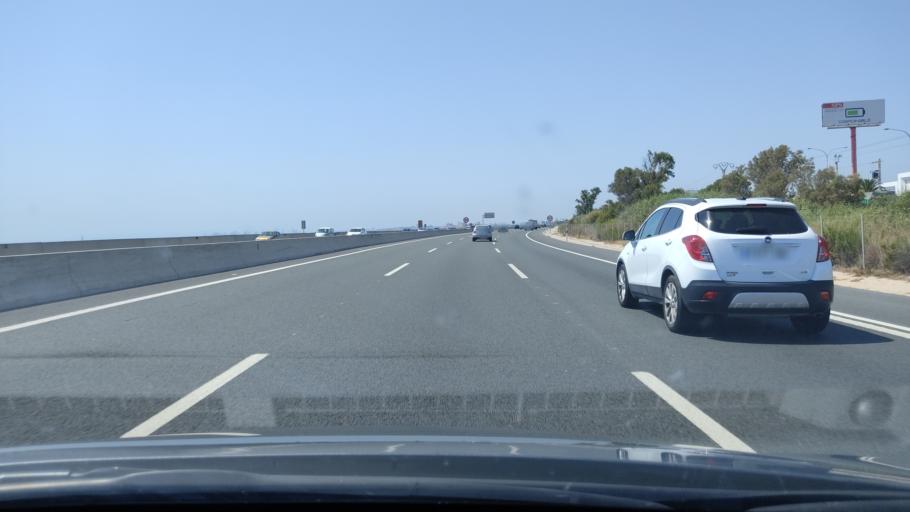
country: ES
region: Valencia
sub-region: Provincia de Valencia
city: Albuixech
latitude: 39.5467
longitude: -0.2990
